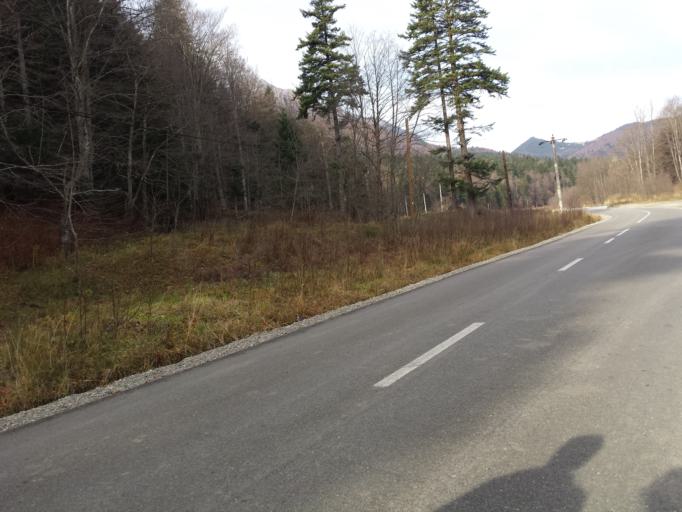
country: RO
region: Prahova
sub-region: Oras Azuga
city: Azuga
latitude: 45.4285
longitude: 25.5362
